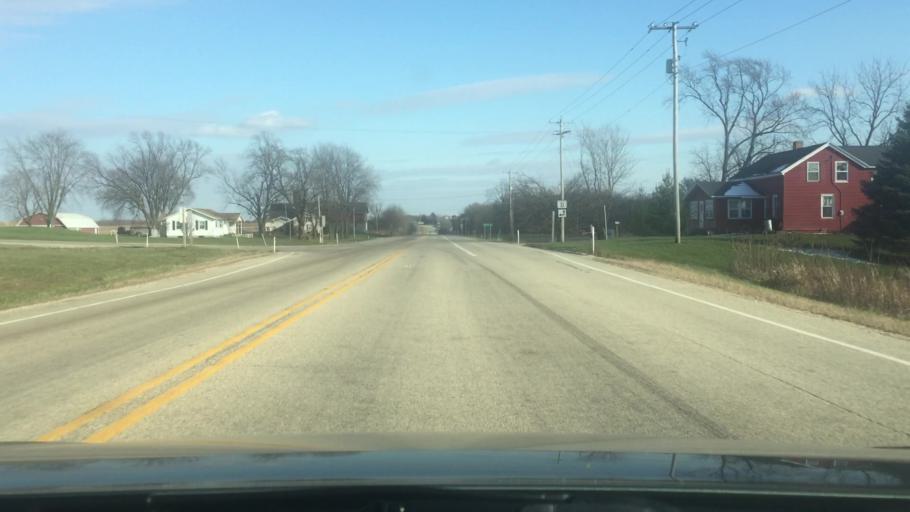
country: US
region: Wisconsin
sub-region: Walworth County
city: Whitewater
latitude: 42.9312
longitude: -88.7003
